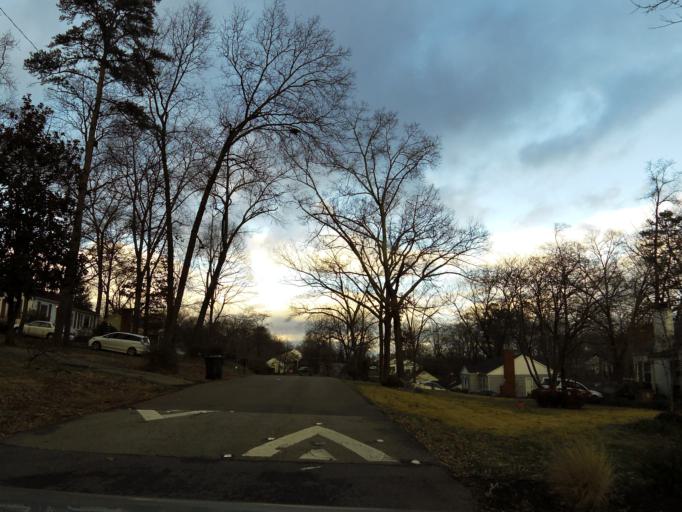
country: US
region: Tennessee
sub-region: Knox County
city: Knoxville
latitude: 36.0103
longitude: -83.8943
